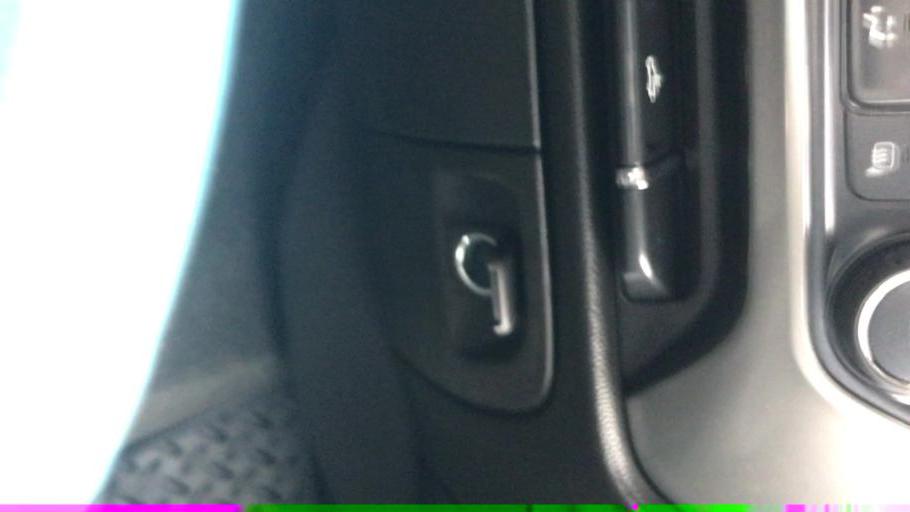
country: US
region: Texas
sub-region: Denton County
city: Flower Mound
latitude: 32.9896
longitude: -97.0617
